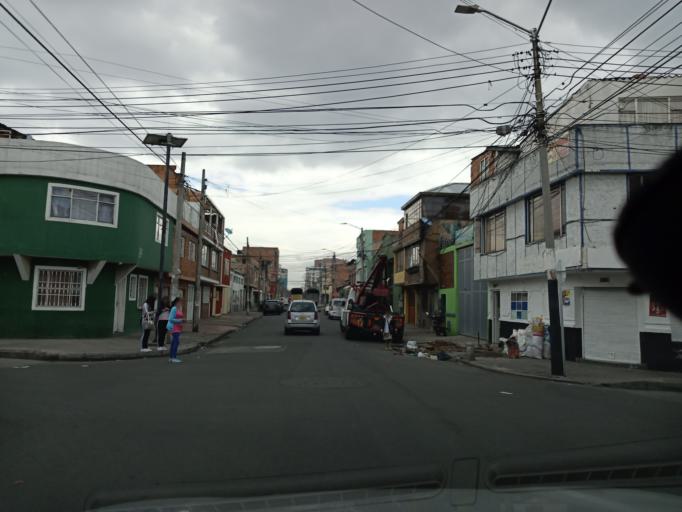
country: CO
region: Bogota D.C.
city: Bogota
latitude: 4.5840
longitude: -74.1147
